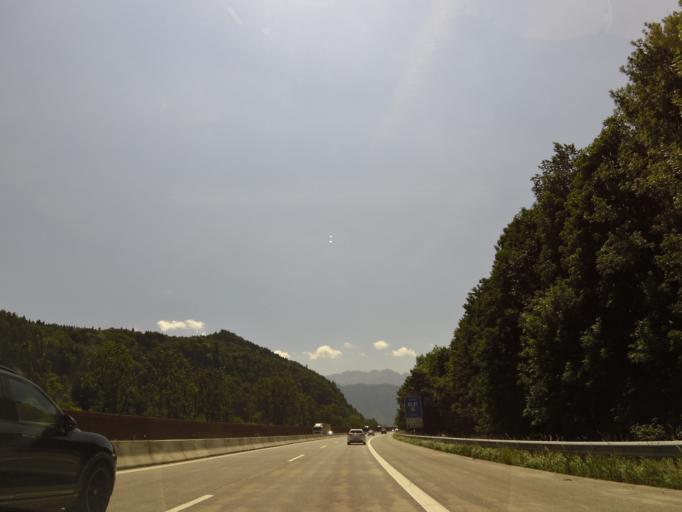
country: AT
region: Tyrol
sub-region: Politischer Bezirk Kufstein
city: Erl
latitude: 47.6675
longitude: 12.1812
